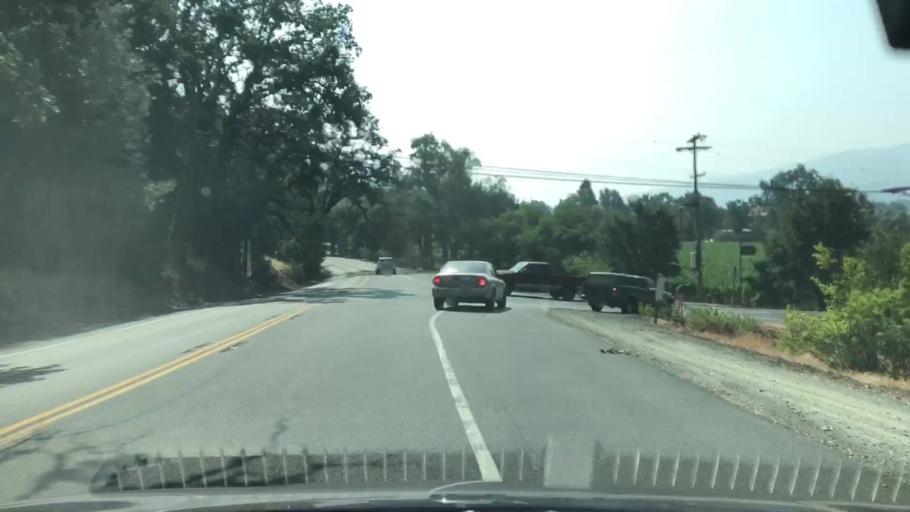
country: US
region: California
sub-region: Napa County
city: Calistoga
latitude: 38.6058
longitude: -122.5958
